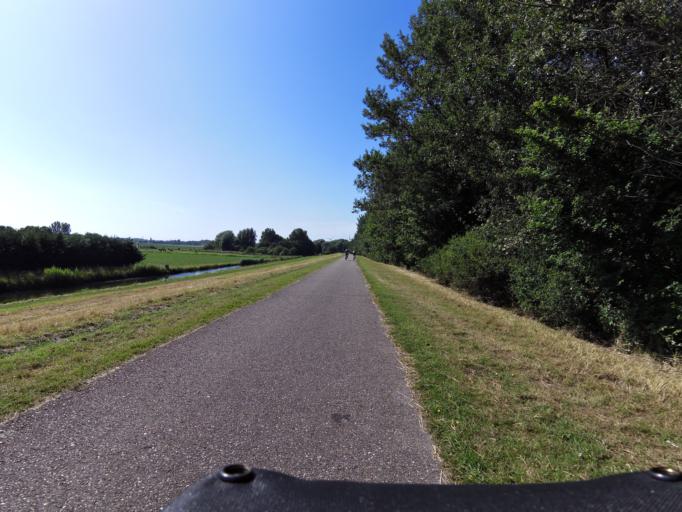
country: NL
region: South Holland
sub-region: Gemeente Brielle
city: Brielle
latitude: 51.9200
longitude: 4.1582
